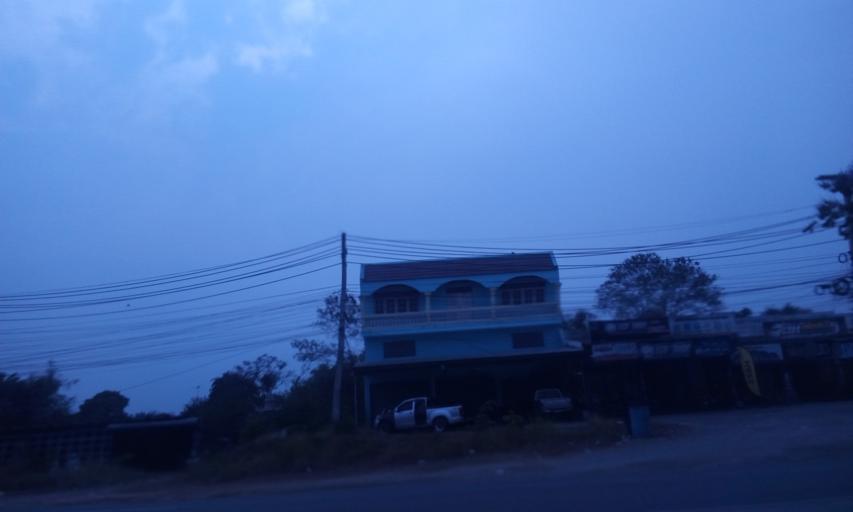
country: TH
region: Chon Buri
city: Ko Chan
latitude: 13.3253
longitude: 101.2702
